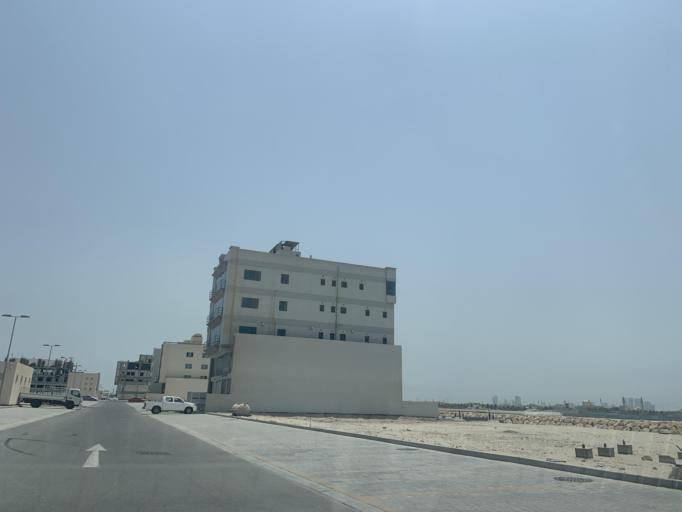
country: BH
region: Muharraq
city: Al Hadd
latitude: 26.2590
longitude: 50.6654
